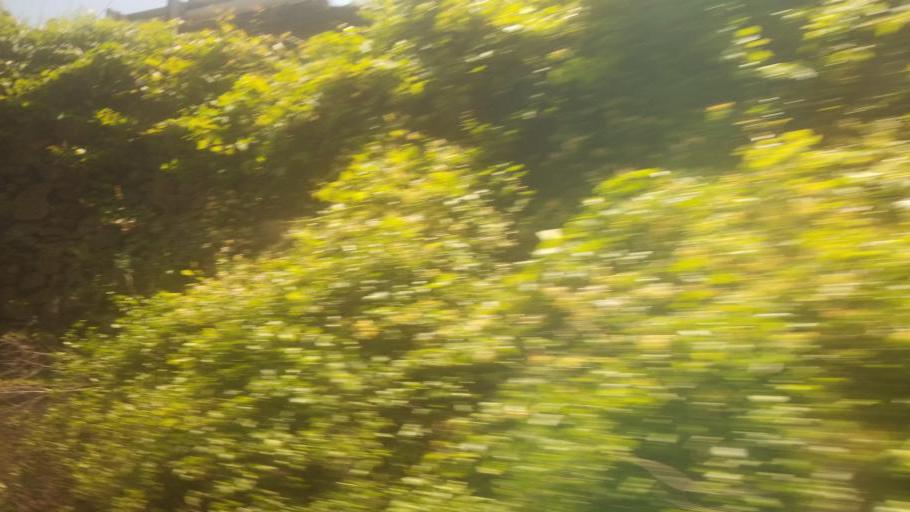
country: US
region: West Virginia
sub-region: Jefferson County
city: Bolivar
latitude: 39.3246
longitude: -77.7221
